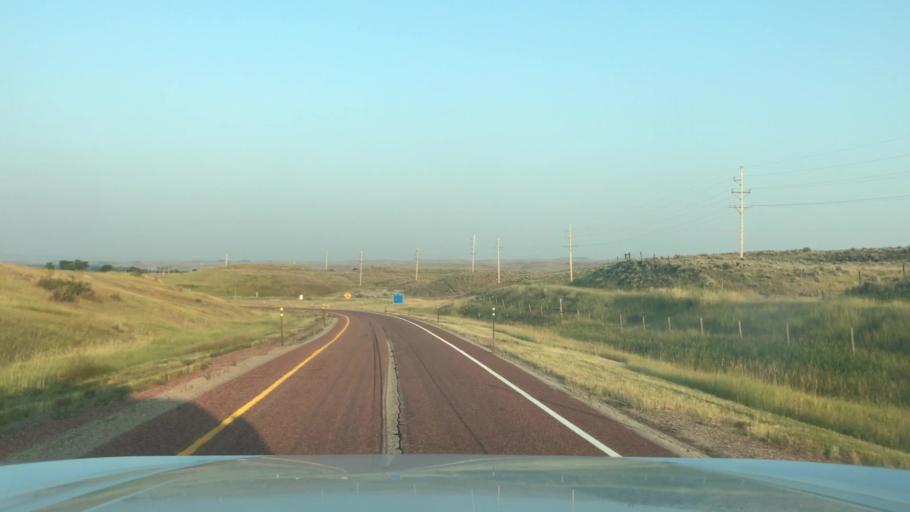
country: US
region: Wyoming
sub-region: Sheridan County
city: Sheridan
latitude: 44.9153
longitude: -107.1563
